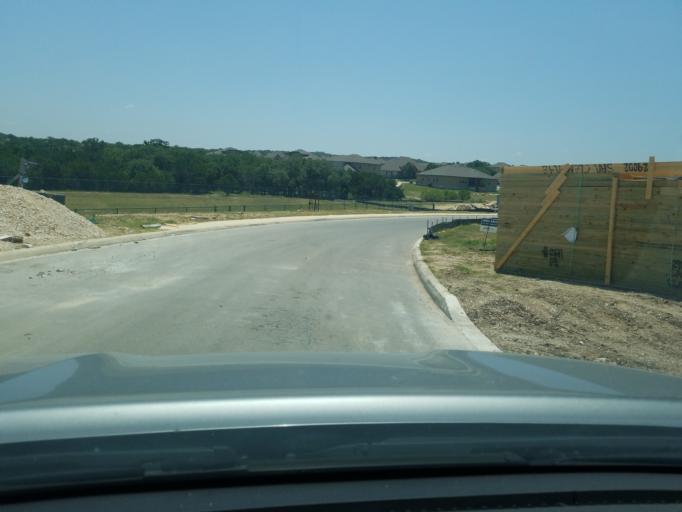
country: US
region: Texas
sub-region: Bexar County
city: Timberwood Park
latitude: 29.7153
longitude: -98.5110
